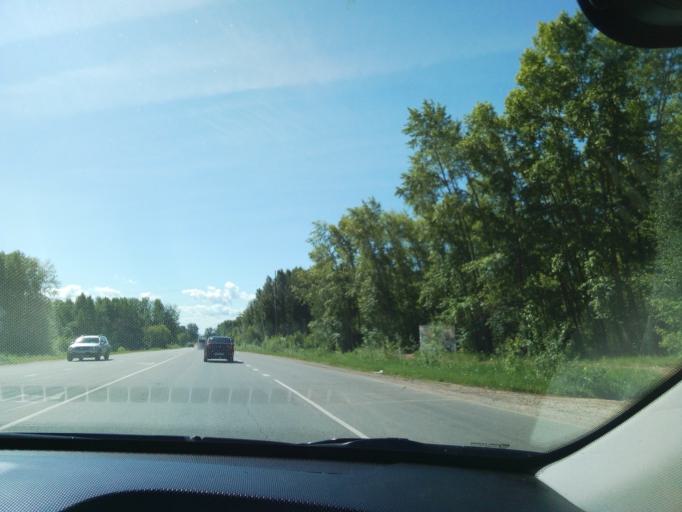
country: RU
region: Chuvashia
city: Novocheboksarsk
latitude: 56.0778
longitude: 47.4964
